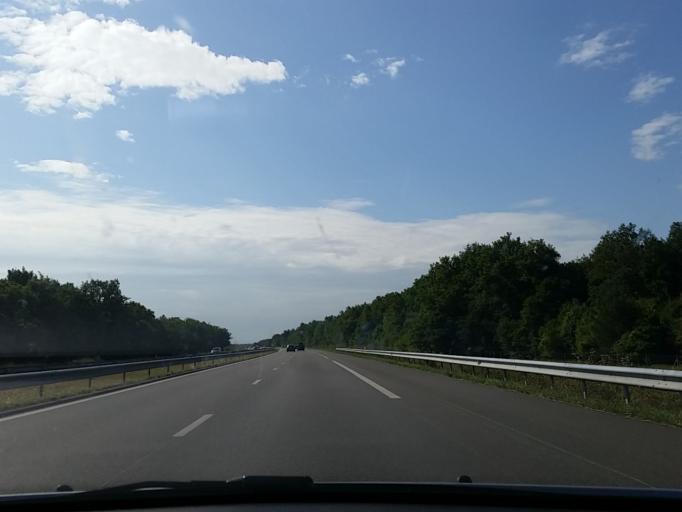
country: FR
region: Centre
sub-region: Departement du Cher
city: Levet
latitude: 46.8851
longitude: 2.4194
